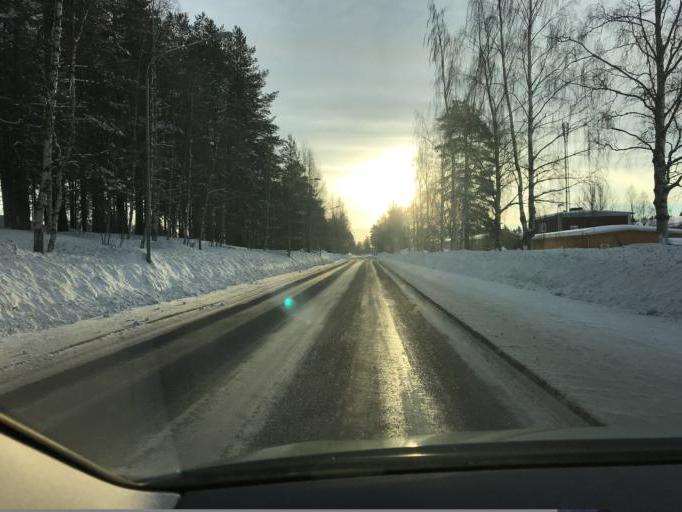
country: SE
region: Norrbotten
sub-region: Lulea Kommun
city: Bergnaset
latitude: 65.6088
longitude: 22.1033
